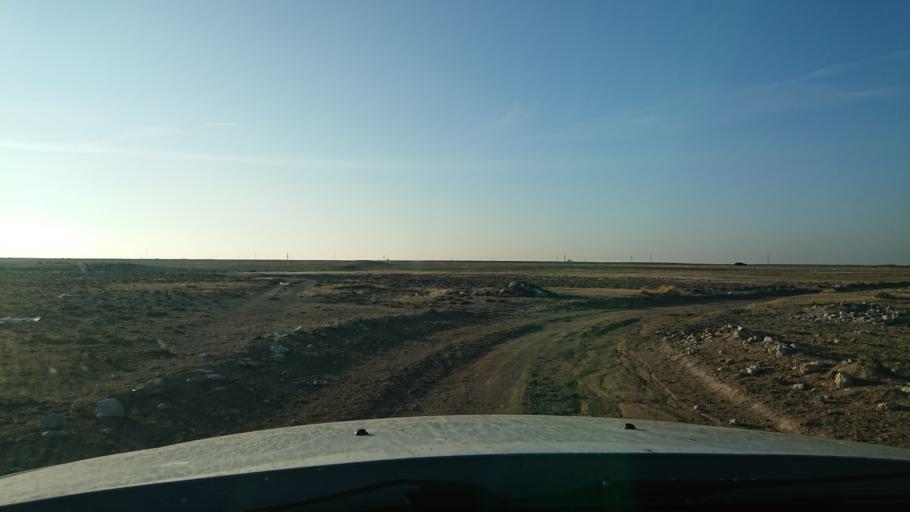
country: TR
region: Aksaray
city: Sultanhani
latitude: 38.2713
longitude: 33.5154
